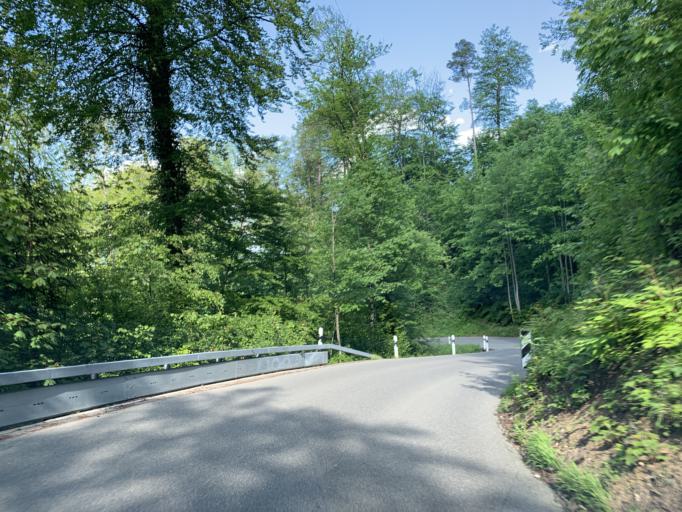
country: CH
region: Zurich
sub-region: Bezirk Winterthur
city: Mattenbach (Kreis 7)
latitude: 47.4608
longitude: 8.7402
